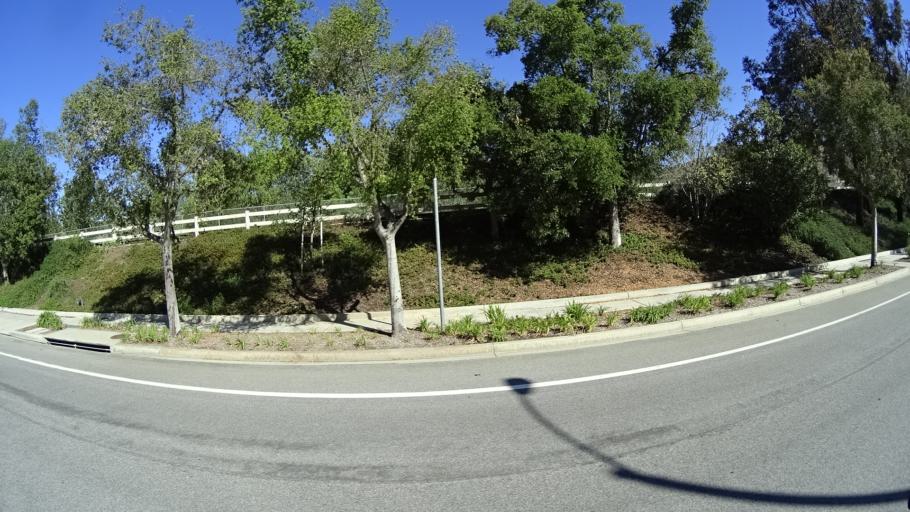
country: US
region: California
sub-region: Ventura County
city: Casa Conejo
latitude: 34.1711
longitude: -118.9880
